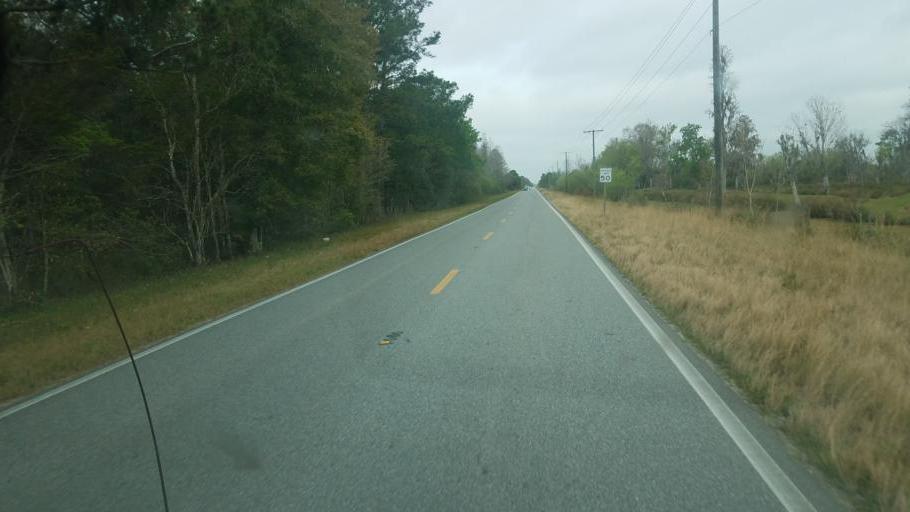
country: US
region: Florida
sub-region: Polk County
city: Polk City
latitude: 28.2590
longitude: -81.9057
